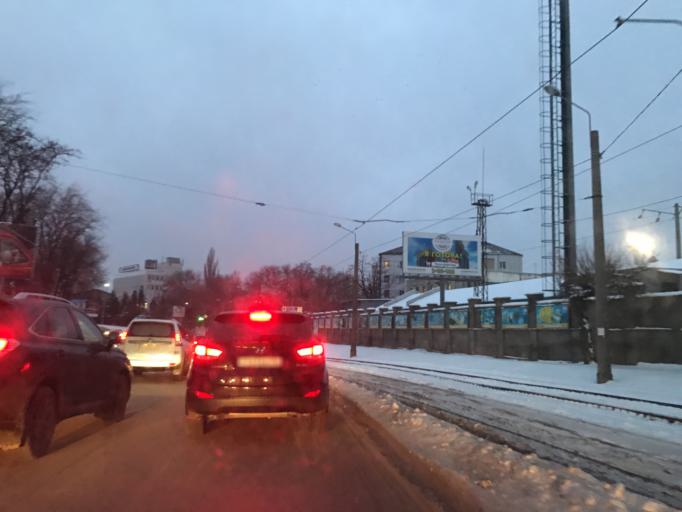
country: RU
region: Rostov
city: Rostov-na-Donu
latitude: 47.2445
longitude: 39.7529
